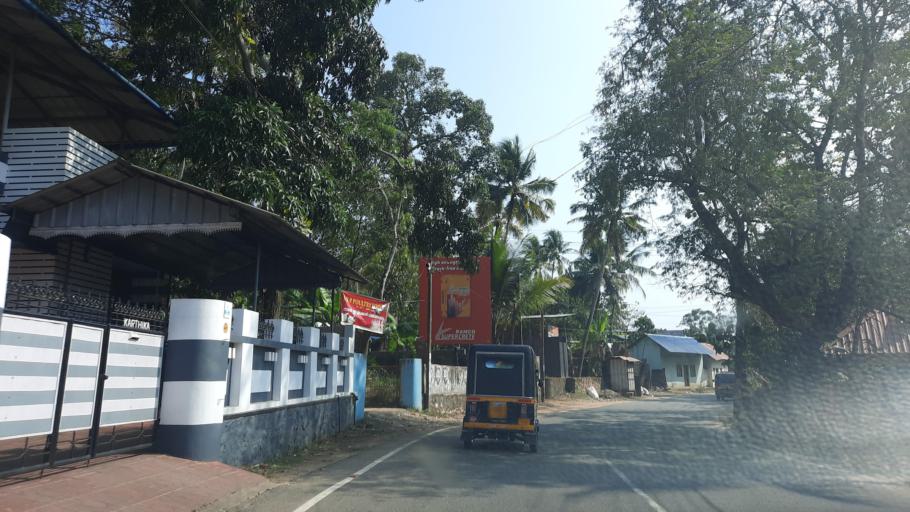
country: IN
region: Kerala
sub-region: Thiruvananthapuram
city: Nedumangad
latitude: 8.5681
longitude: 76.9232
